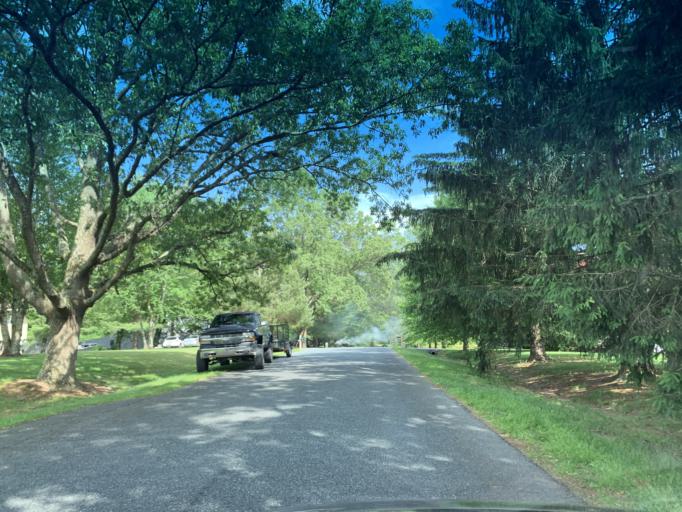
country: US
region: Maryland
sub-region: Harford County
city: Jarrettsville
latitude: 39.6010
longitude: -76.4634
